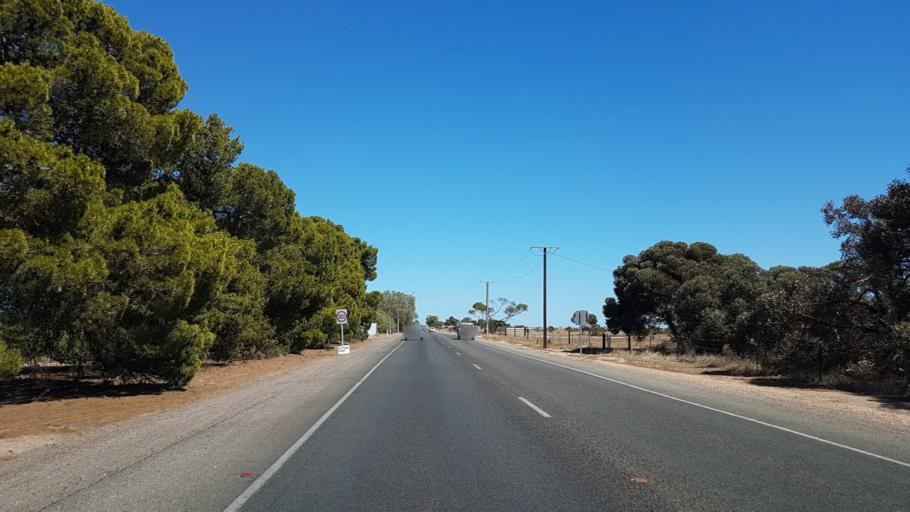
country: AU
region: South Australia
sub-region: Copper Coast
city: Kadina
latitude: -33.9528
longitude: 137.6814
